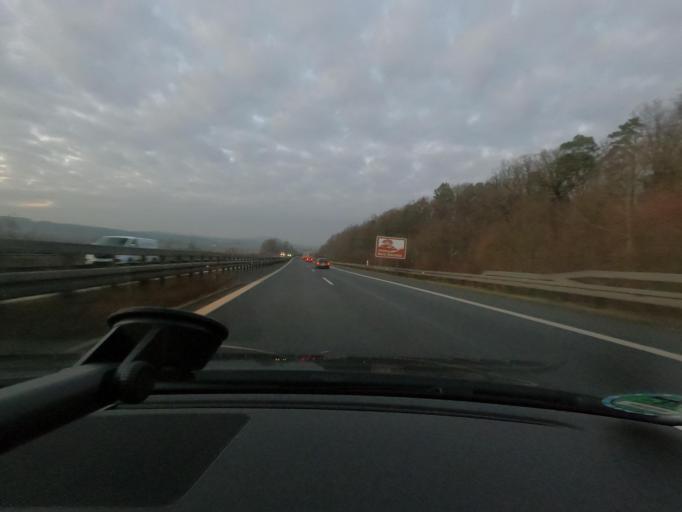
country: DE
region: Bavaria
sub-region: Upper Franconia
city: Ebensfeld
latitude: 50.0409
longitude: 10.9585
